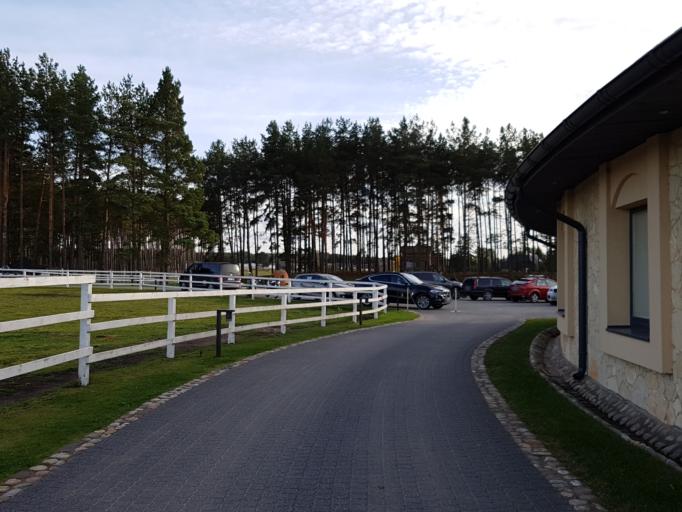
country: LT
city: Moletai
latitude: 55.0405
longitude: 25.4139
